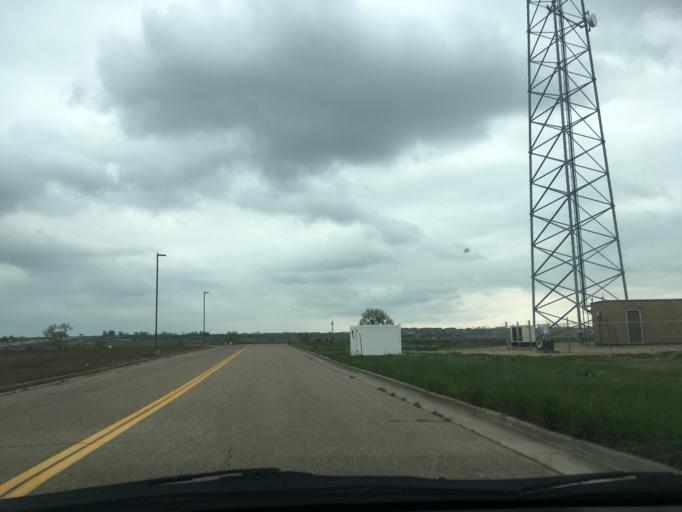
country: US
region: Colorado
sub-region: Weld County
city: Mead
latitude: 40.1693
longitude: -104.9748
